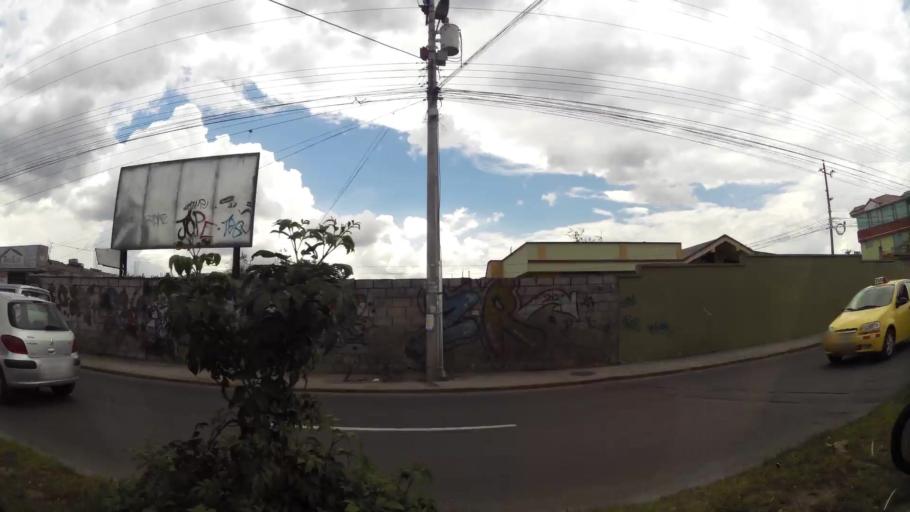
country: EC
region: Pichincha
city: Quito
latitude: -0.0866
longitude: -78.4233
